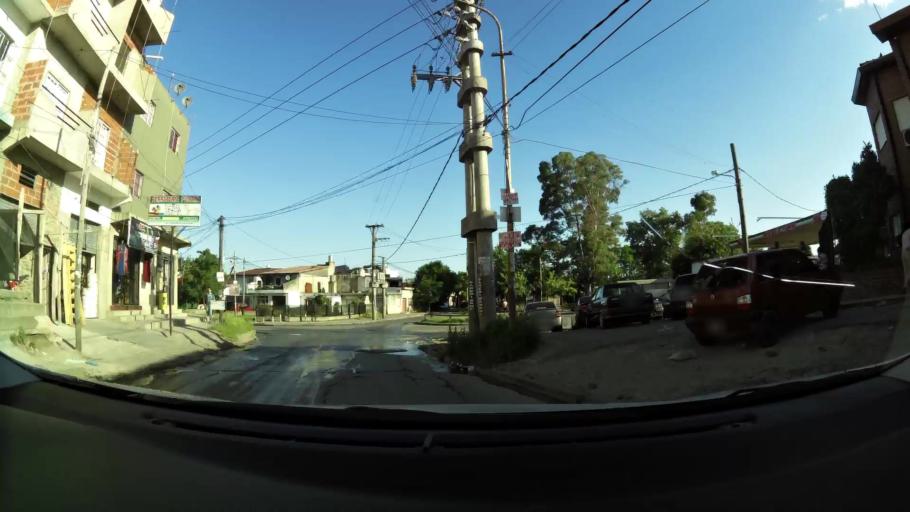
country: AR
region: Buenos Aires F.D.
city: Villa Lugano
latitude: -34.7047
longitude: -58.4794
